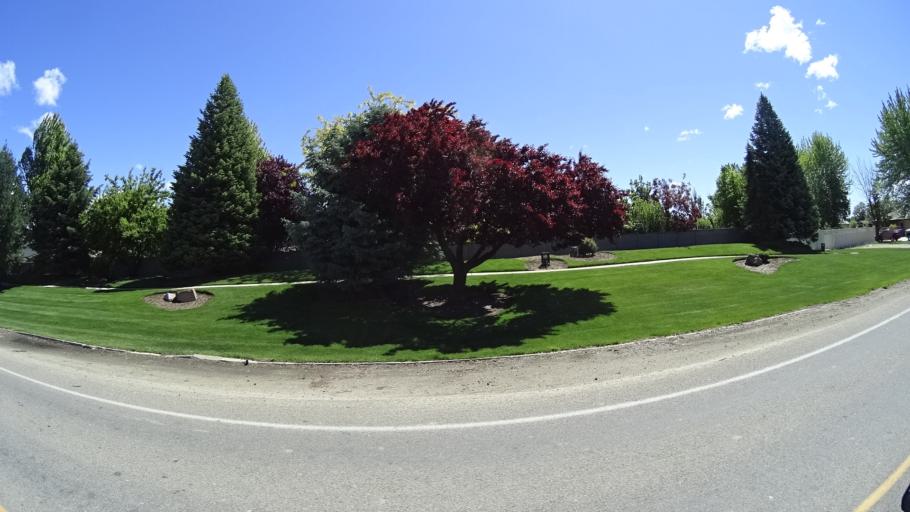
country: US
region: Idaho
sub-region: Ada County
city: Meridian
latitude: 43.6525
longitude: -116.3746
